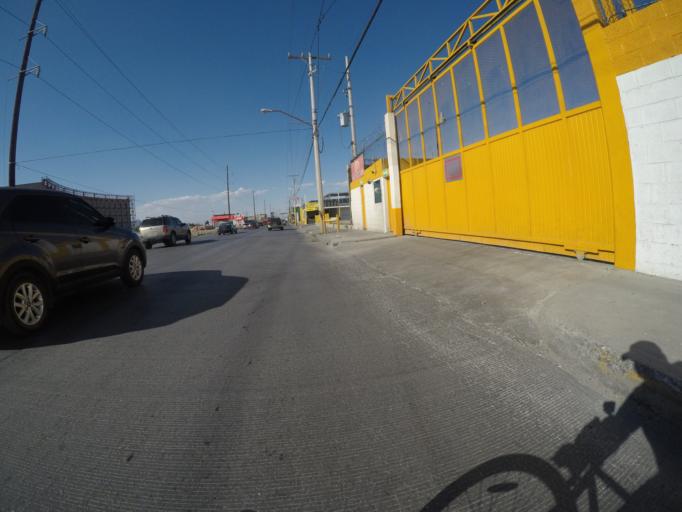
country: MX
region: Chihuahua
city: Ciudad Juarez
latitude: 31.7177
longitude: -106.4442
